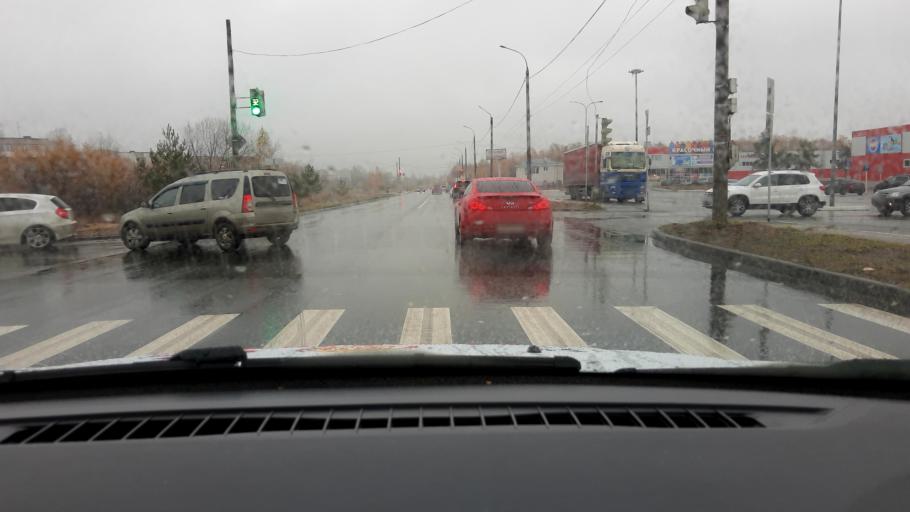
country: RU
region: Nizjnij Novgorod
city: Dzerzhinsk
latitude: 56.2407
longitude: 43.4084
